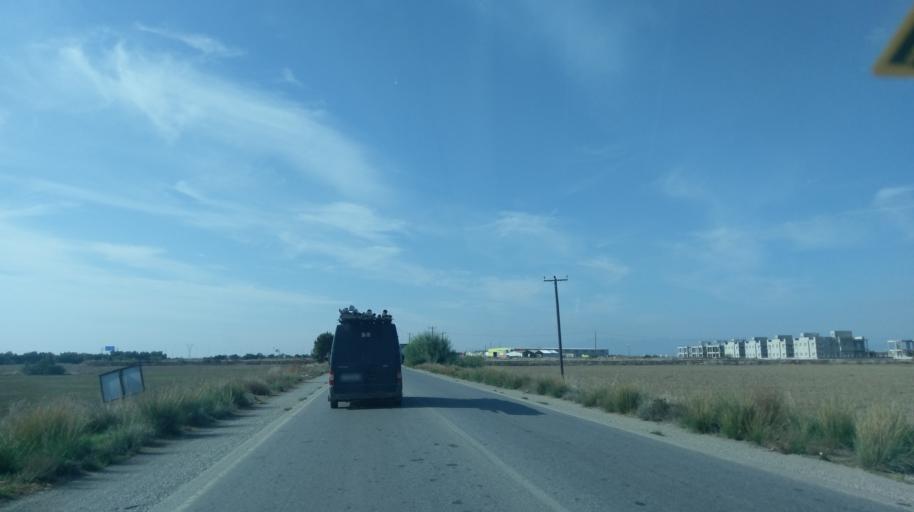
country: CY
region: Ammochostos
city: Acheritou
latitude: 35.1529
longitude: 33.8532
